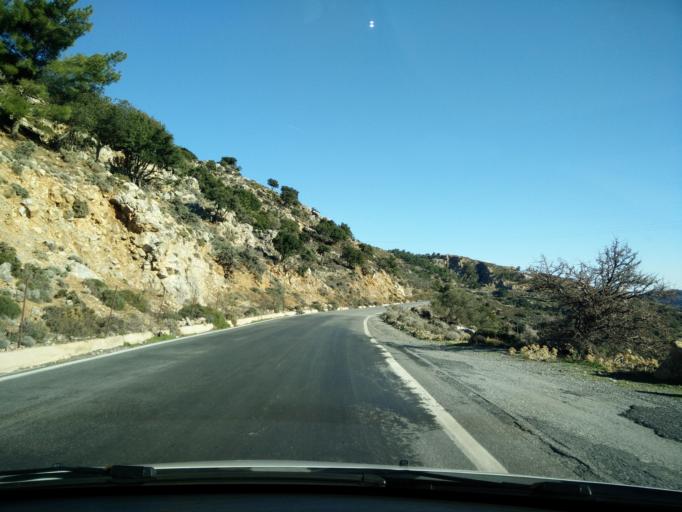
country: GR
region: Crete
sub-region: Nomos Irakleiou
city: Kastelli
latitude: 35.0451
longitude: 25.4301
